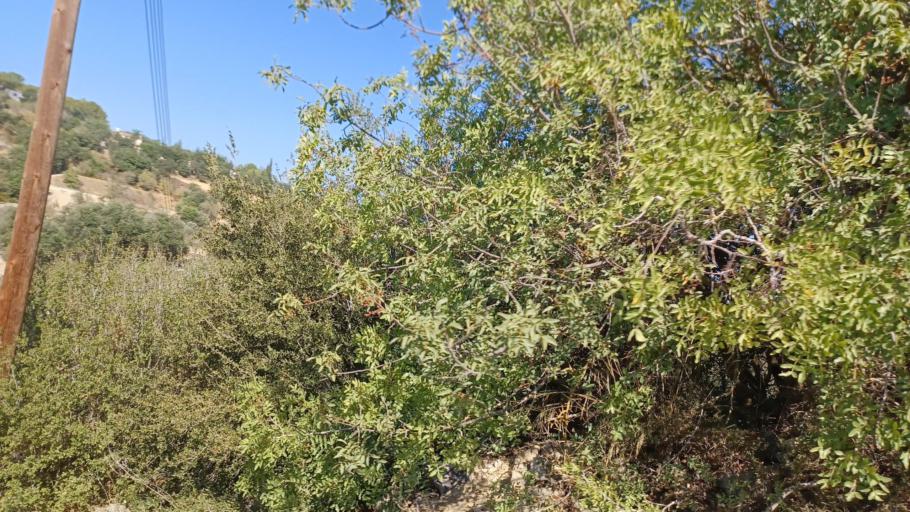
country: CY
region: Pafos
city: Tala
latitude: 34.9252
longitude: 32.4824
